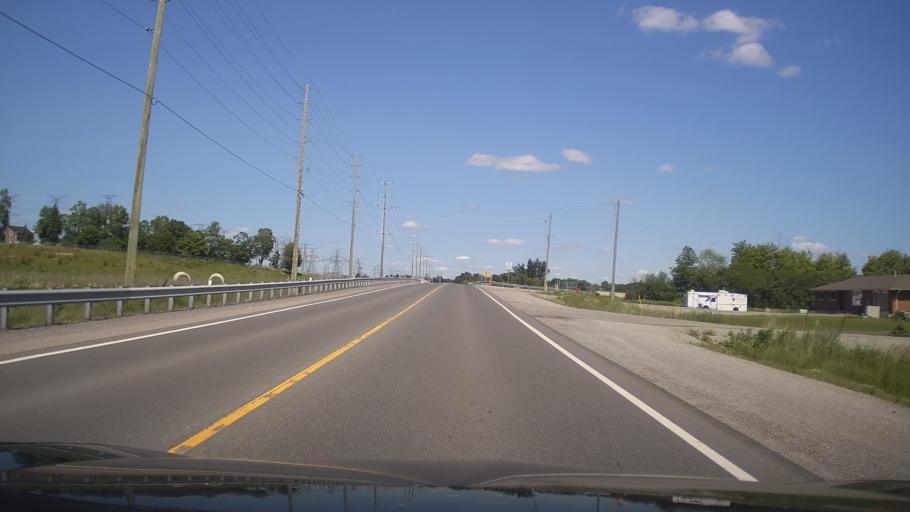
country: CA
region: Ontario
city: Oshawa
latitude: 43.9780
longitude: -78.8577
